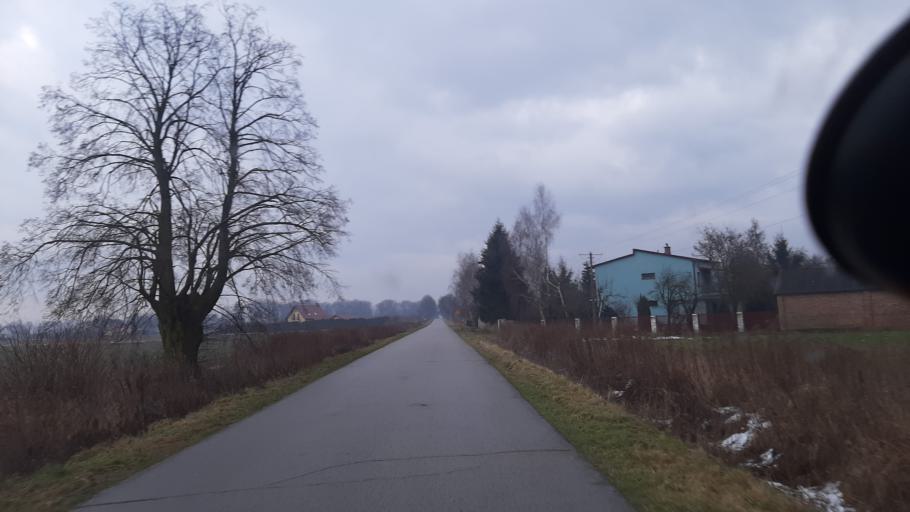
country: PL
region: Lublin Voivodeship
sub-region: Powiat lubelski
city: Lublin
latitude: 51.3372
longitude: 22.5439
